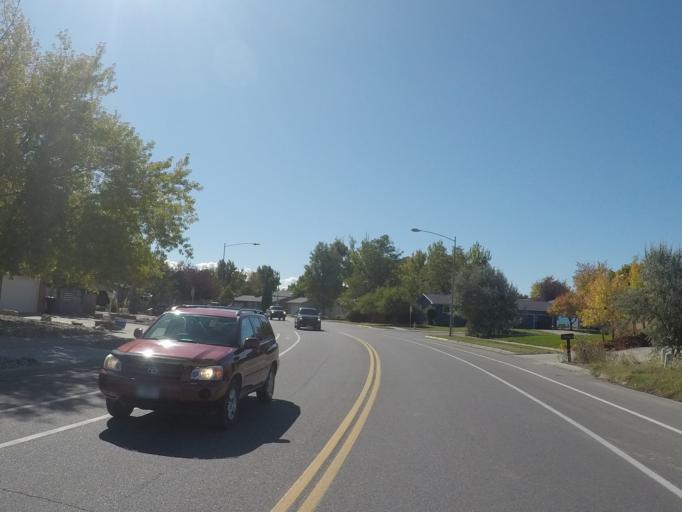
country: US
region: Montana
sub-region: Yellowstone County
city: Billings
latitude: 45.8131
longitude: -108.4973
